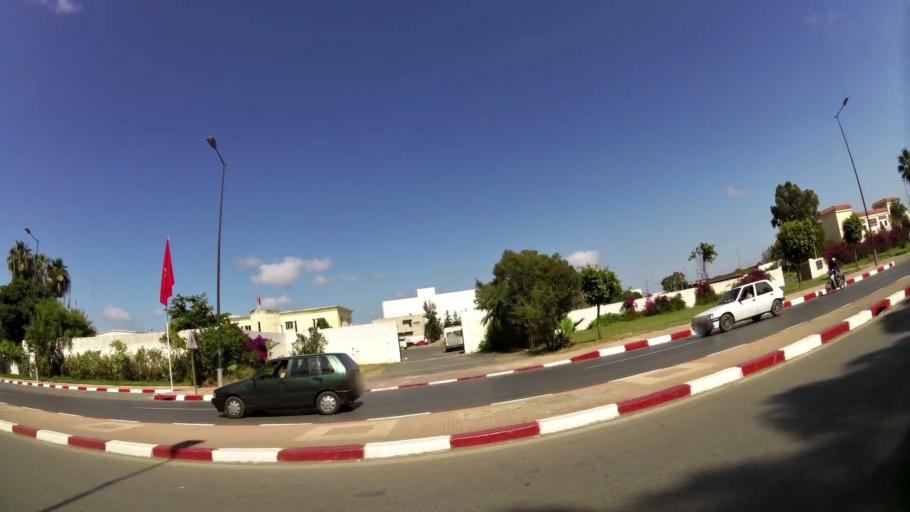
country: MA
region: Rabat-Sale-Zemmour-Zaer
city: Sale
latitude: 34.0368
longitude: -6.7755
